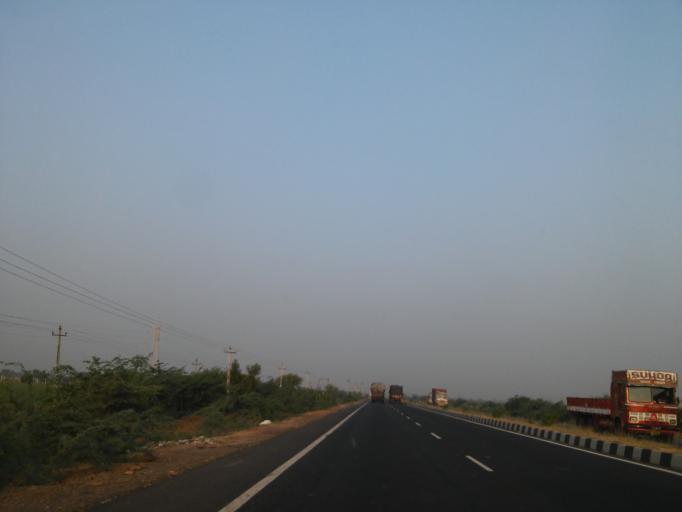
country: IN
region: Gujarat
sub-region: Kachchh
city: Bhachau
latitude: 23.2771
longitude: 70.6064
